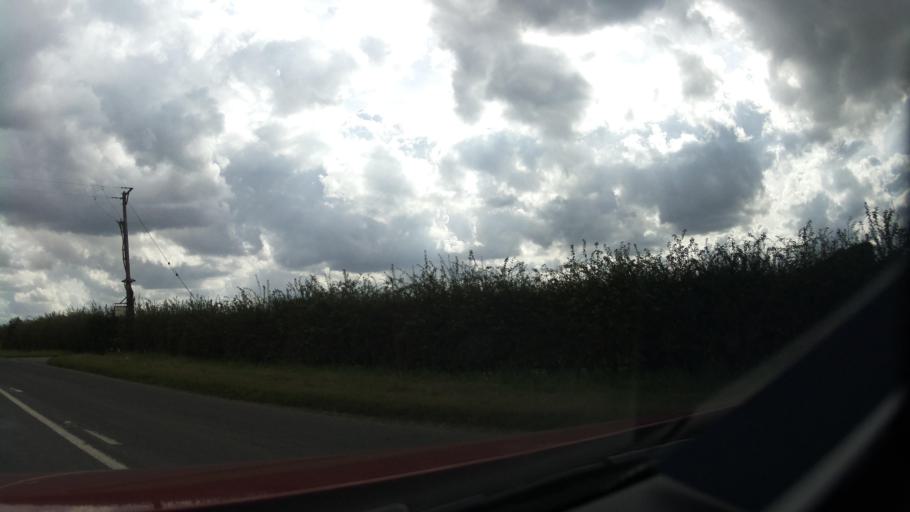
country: GB
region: England
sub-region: North Yorkshire
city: Ripon
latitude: 54.1723
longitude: -1.5526
